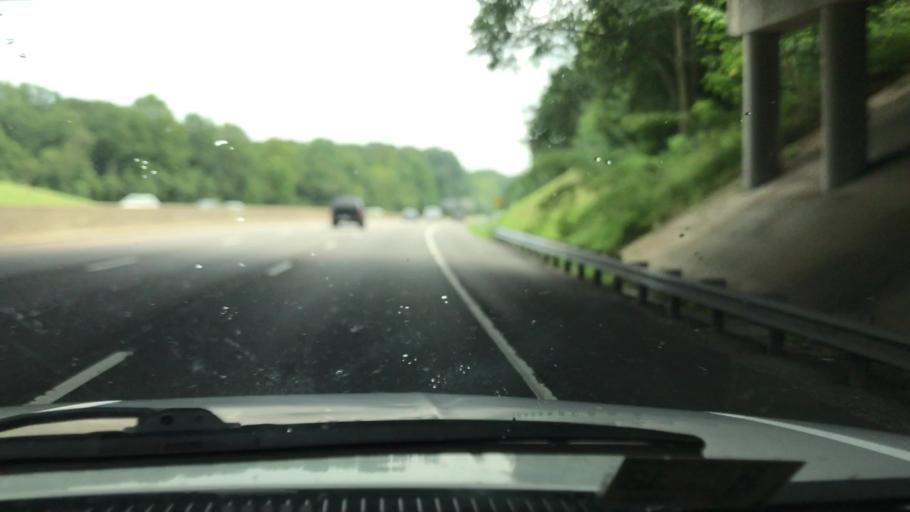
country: US
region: Virginia
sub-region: Chesterfield County
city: Bensley
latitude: 37.4617
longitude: -77.4980
